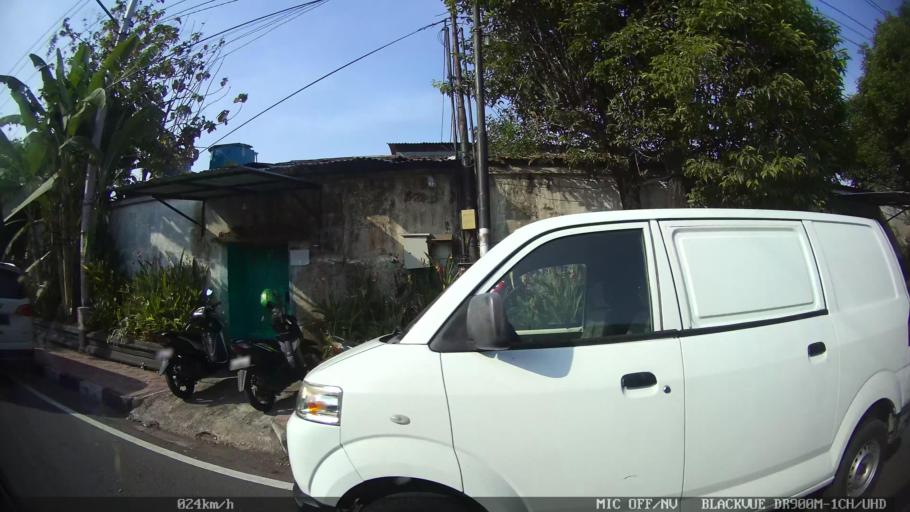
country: ID
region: Daerah Istimewa Yogyakarta
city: Yogyakarta
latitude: -7.7886
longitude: 110.3631
